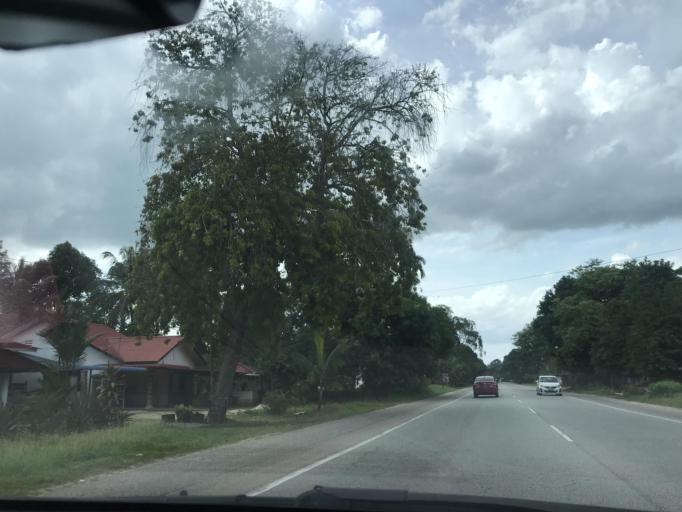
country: MY
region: Kelantan
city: Kampong Pangkal Kalong
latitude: 5.9332
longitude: 102.1913
